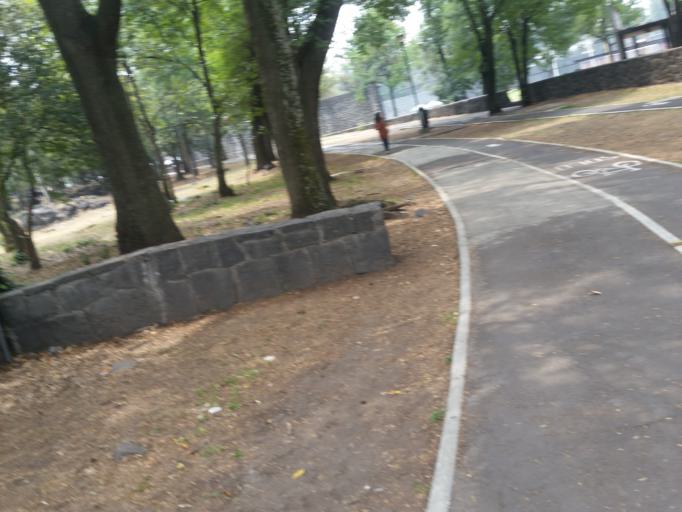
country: MX
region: Mexico City
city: Magdalena Contreras
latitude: 19.3249
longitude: -99.1865
